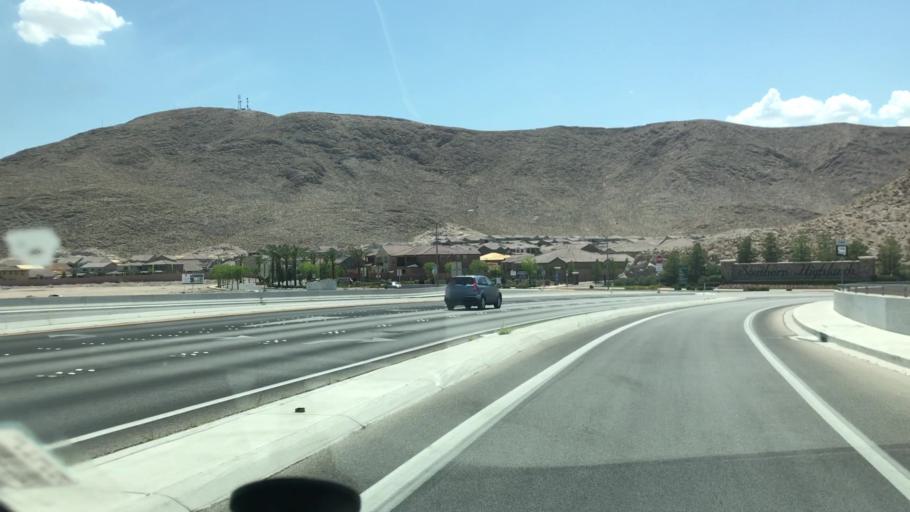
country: US
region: Nevada
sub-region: Clark County
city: Enterprise
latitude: 35.9613
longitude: -115.1834
